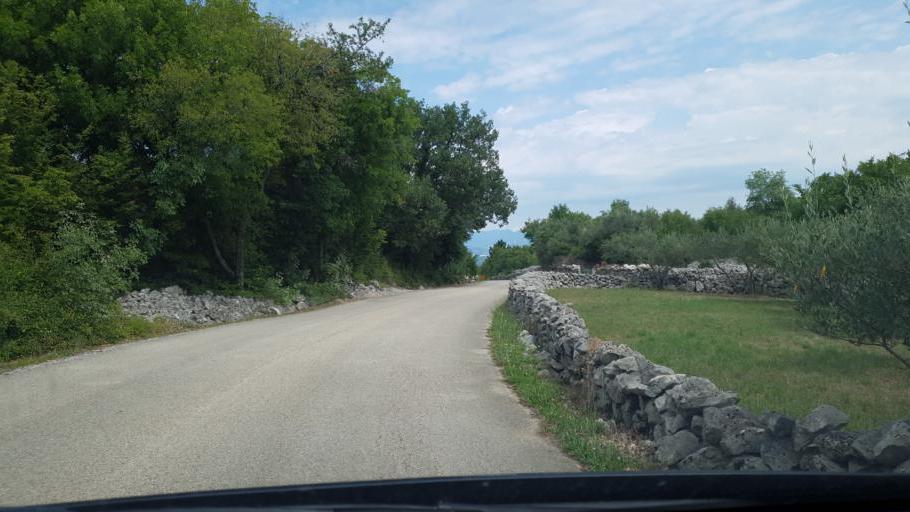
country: HR
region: Primorsko-Goranska
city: Njivice
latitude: 45.1308
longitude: 14.5833
